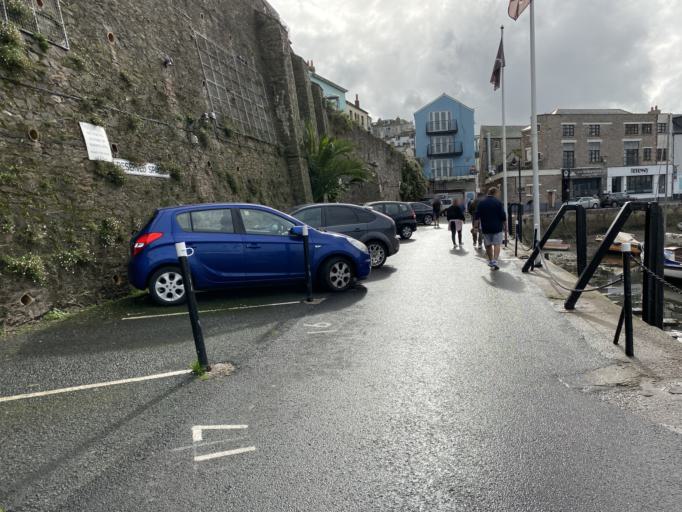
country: GB
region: England
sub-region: Borough of Torbay
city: Brixham
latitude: 50.3962
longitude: -3.5113
